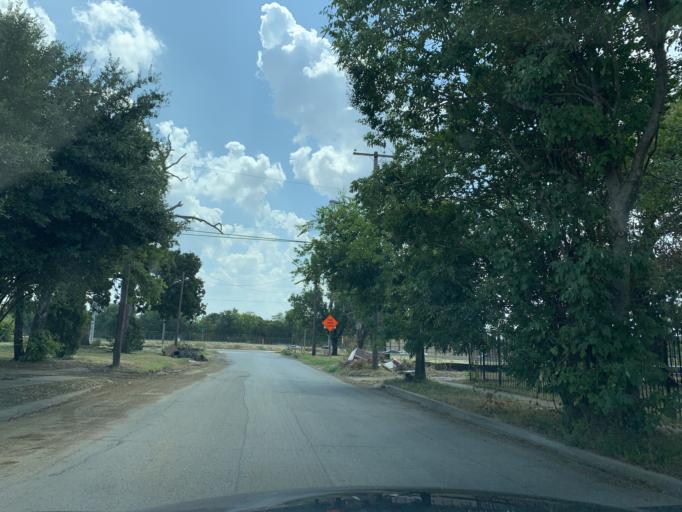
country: US
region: Texas
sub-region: Dallas County
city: Dallas
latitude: 32.7438
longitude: -96.8180
